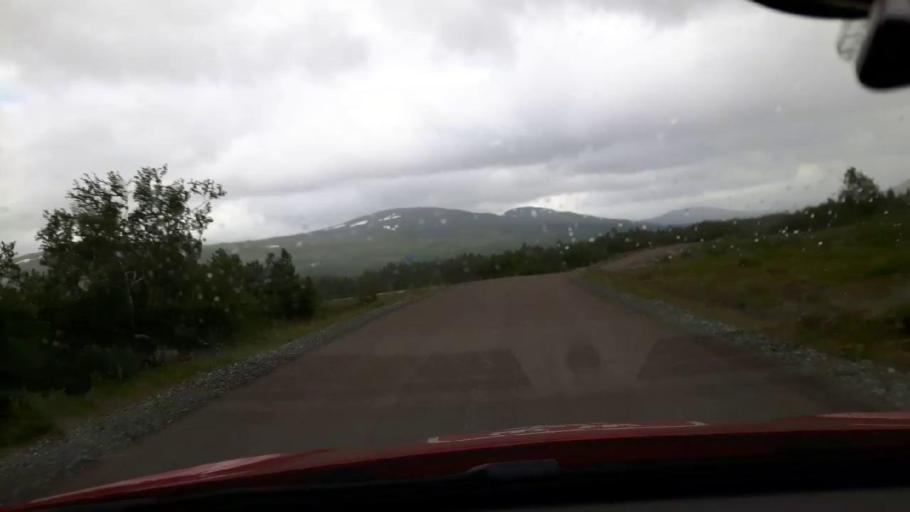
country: SE
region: Jaemtland
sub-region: Are Kommun
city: Are
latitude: 63.2364
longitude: 12.4307
